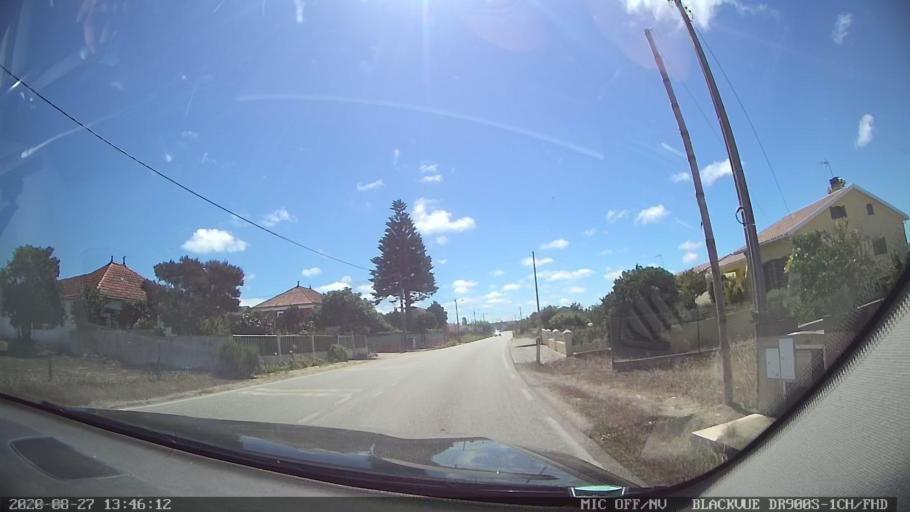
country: PT
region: Coimbra
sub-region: Mira
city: Mira
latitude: 40.3981
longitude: -8.7356
